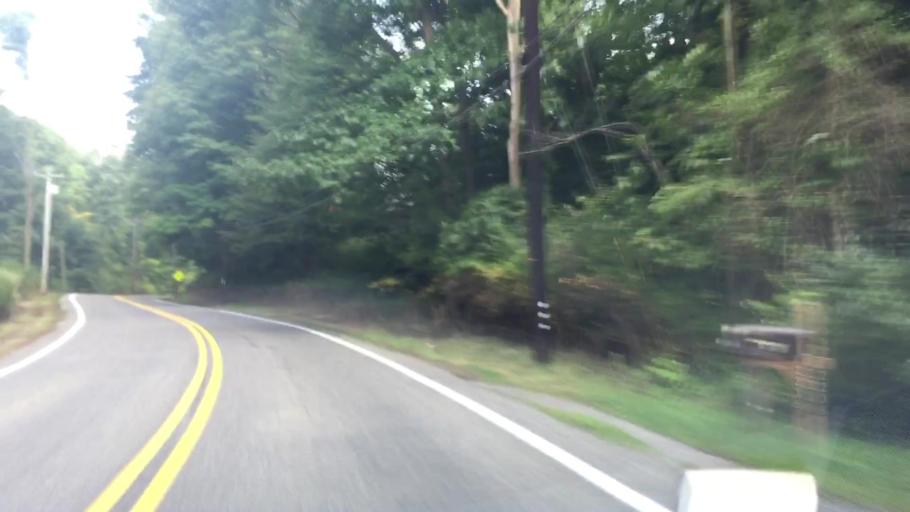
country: US
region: Pennsylvania
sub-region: Allegheny County
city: Franklin Park
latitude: 40.5637
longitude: -80.0909
